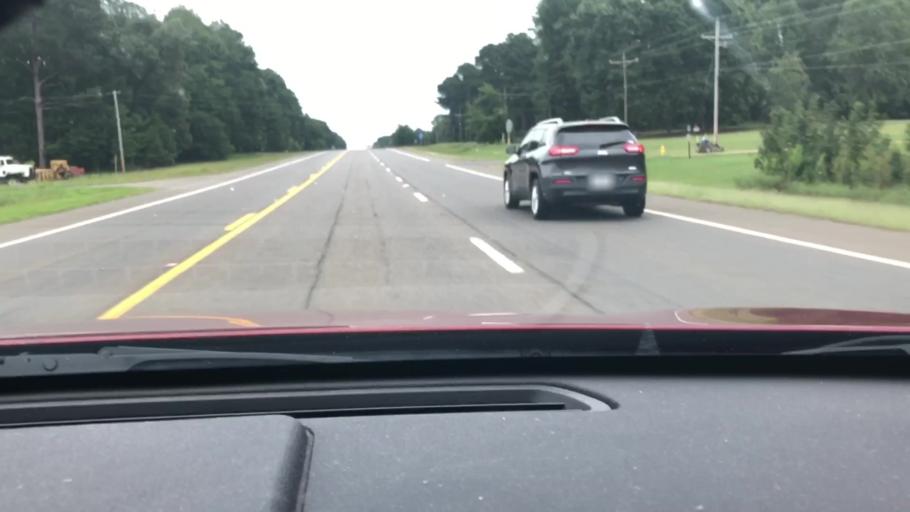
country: US
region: Arkansas
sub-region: Lafayette County
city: Stamps
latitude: 33.3640
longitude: -93.4702
